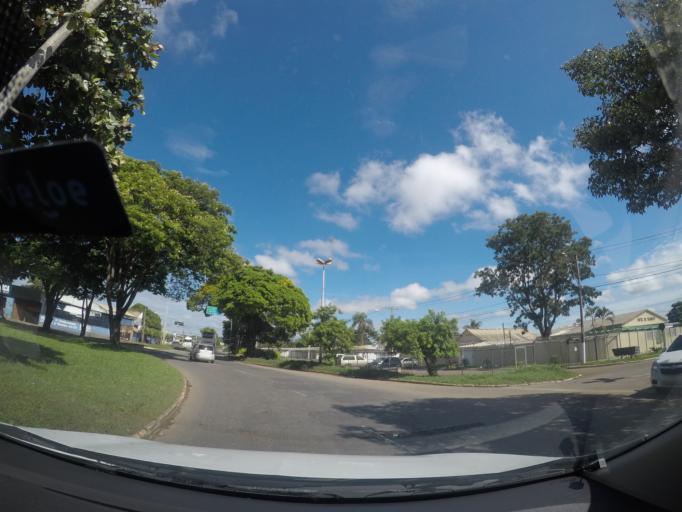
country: BR
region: Goias
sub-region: Goiania
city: Goiania
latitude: -16.6239
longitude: -49.2307
